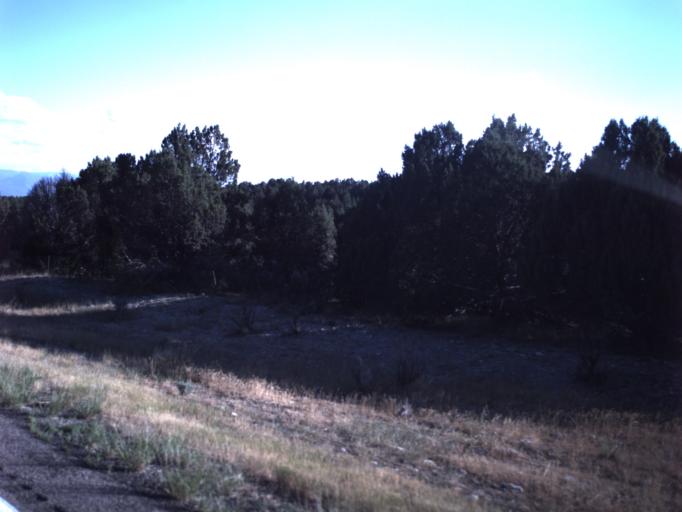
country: US
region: Utah
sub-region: Sanpete County
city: Fairview
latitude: 39.6637
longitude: -111.4525
